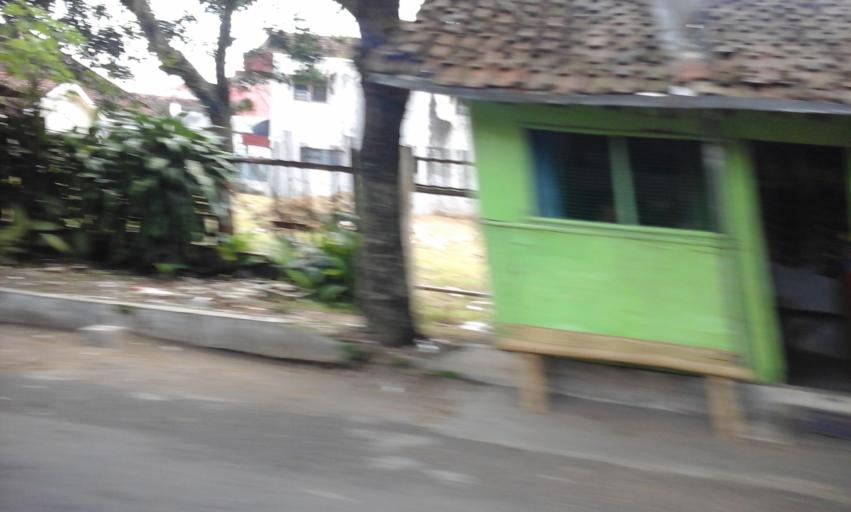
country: ID
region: East Java
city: Kaliwates
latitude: -8.1777
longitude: 113.6775
